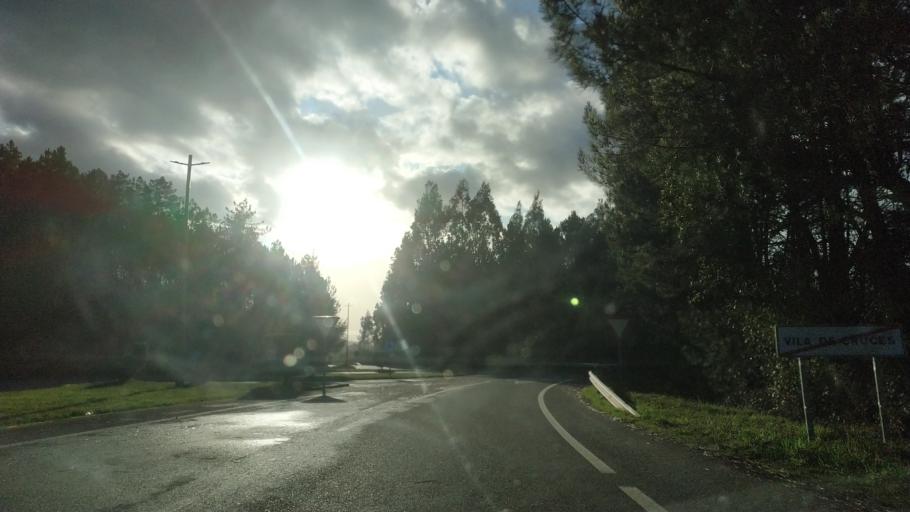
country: ES
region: Galicia
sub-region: Provincia de Pontevedra
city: Silleda
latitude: 42.7889
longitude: -8.1647
